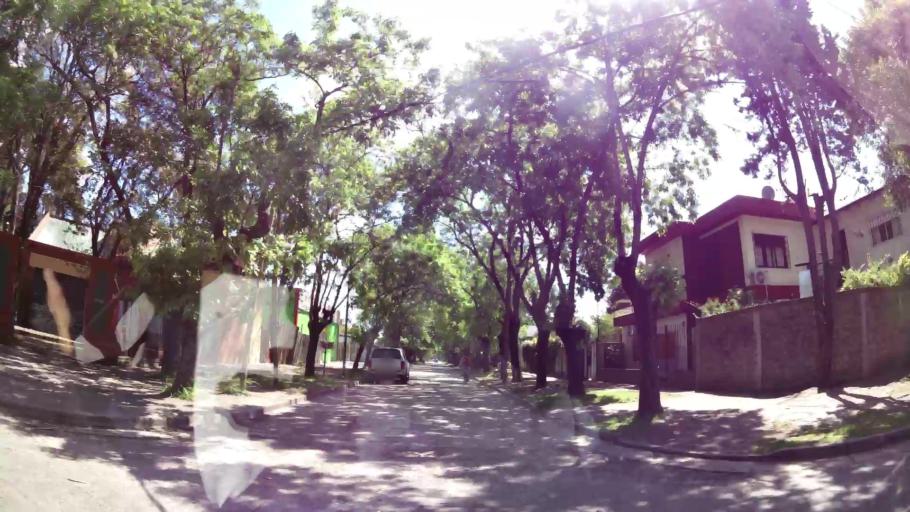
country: AR
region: Buenos Aires
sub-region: Partido de Quilmes
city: Quilmes
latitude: -34.8137
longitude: -58.2705
